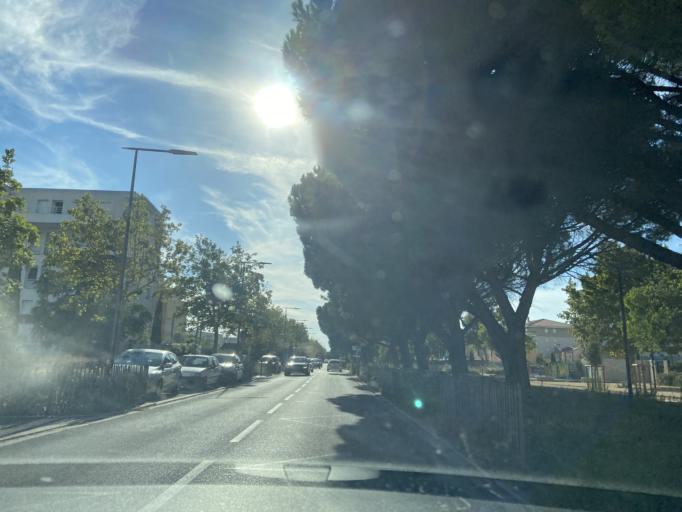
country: FR
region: Provence-Alpes-Cote d'Azur
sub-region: Departement des Bouches-du-Rhone
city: Miramas
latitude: 43.5876
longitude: 5.0021
